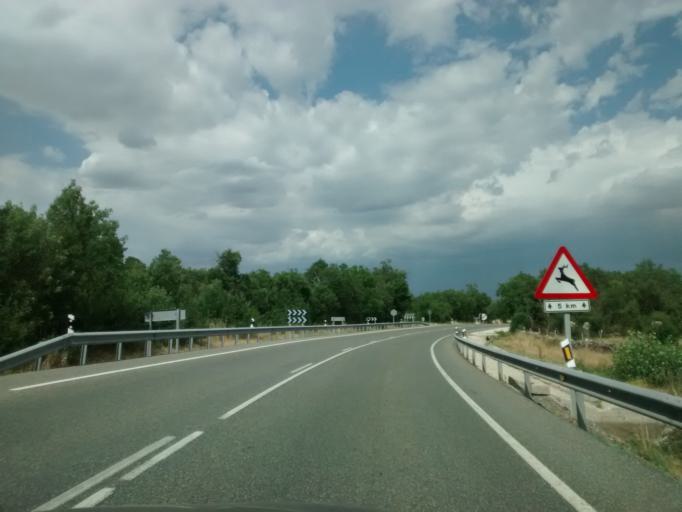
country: ES
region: Castille and Leon
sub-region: Provincia de Segovia
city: Gallegos
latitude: 41.0882
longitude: -3.7894
